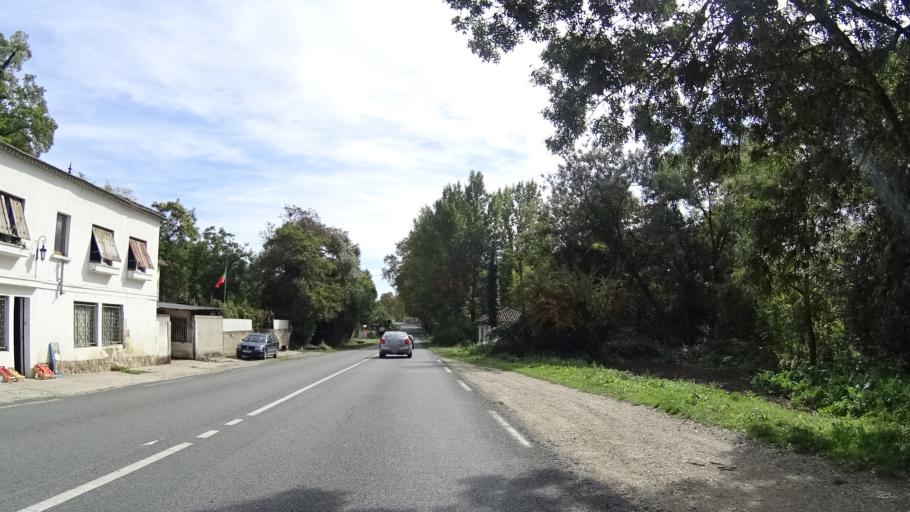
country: FR
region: Aquitaine
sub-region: Departement du Lot-et-Garonne
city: Castelculier
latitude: 44.1552
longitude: 0.7347
